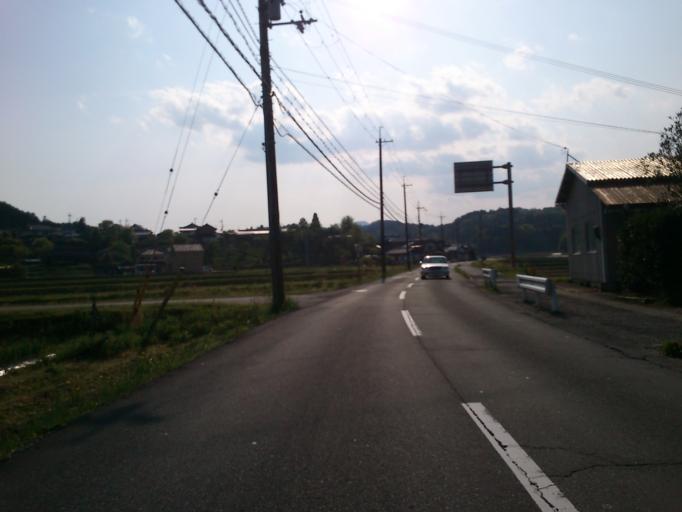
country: JP
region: Kyoto
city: Fukuchiyama
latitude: 35.2922
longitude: 135.0789
